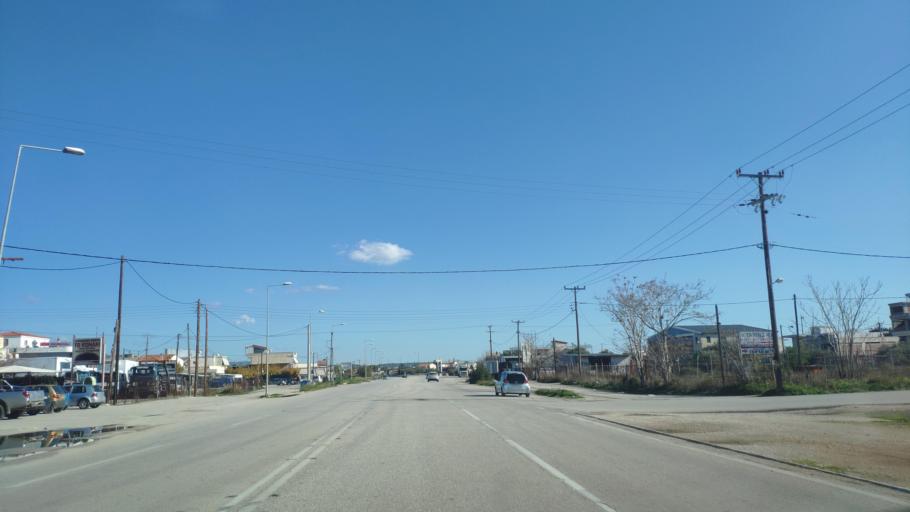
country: GR
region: Peloponnese
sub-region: Nomos Korinthias
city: Korinthos
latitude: 37.9342
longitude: 22.9390
